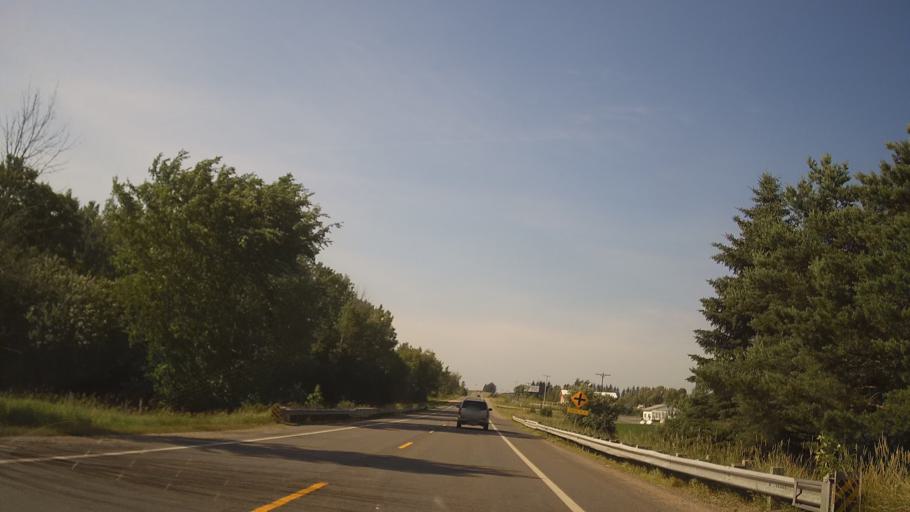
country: US
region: Michigan
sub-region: Ogemaw County
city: West Branch
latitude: 44.3471
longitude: -84.1259
